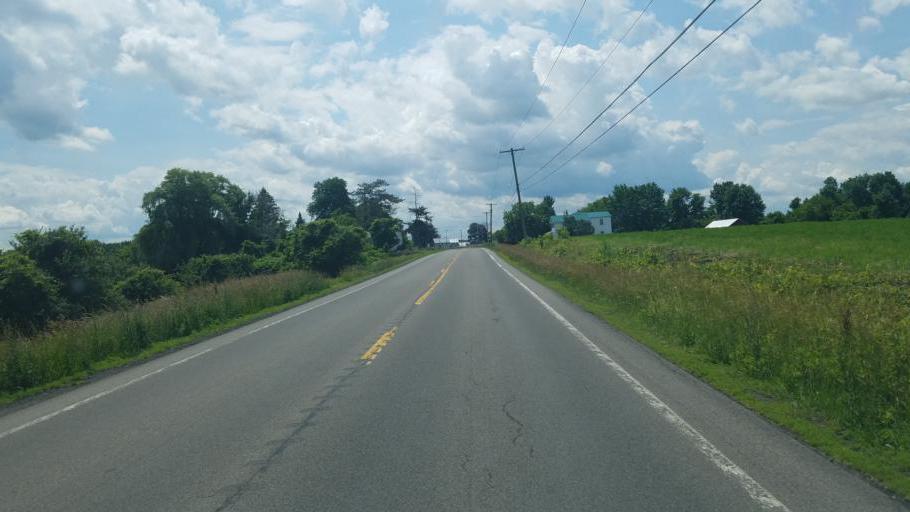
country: US
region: New York
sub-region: Wayne County
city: Clyde
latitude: 43.1093
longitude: -76.8700
